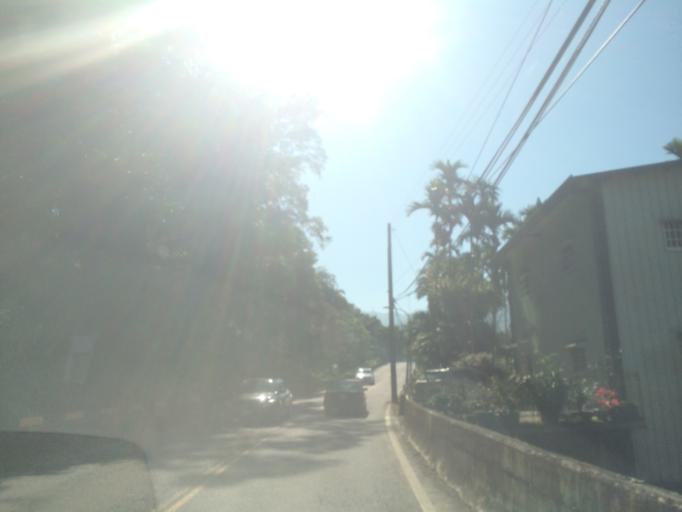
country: TW
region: Taiwan
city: Lugu
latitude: 23.7225
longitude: 120.7780
